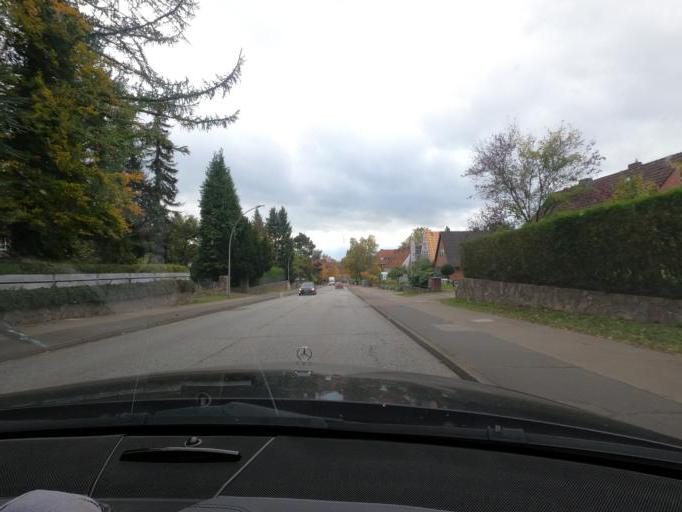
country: DE
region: Schleswig-Holstein
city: Geesthacht
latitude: 53.4442
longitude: 10.3728
